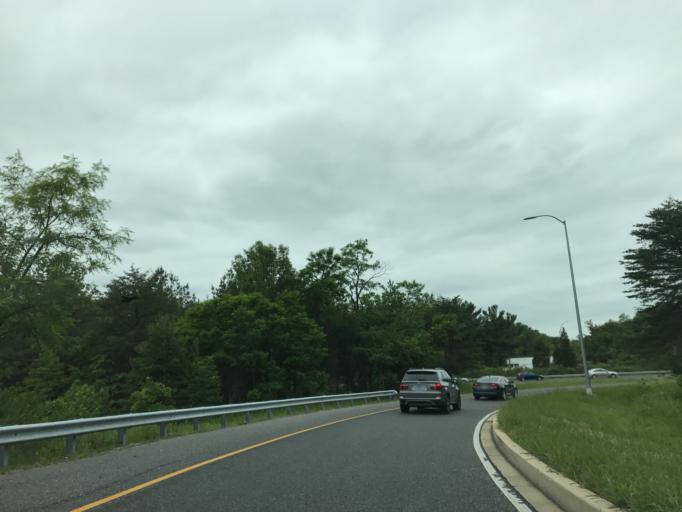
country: US
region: Maryland
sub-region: Howard County
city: West Elkridge
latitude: 39.1951
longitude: -76.7669
